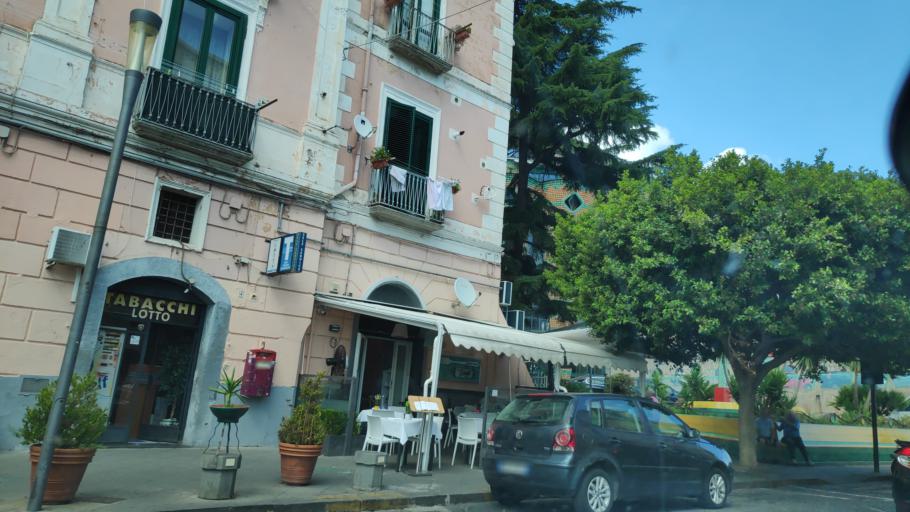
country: IT
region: Campania
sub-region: Provincia di Salerno
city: Vietri sul Mare
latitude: 40.6710
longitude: 14.7305
